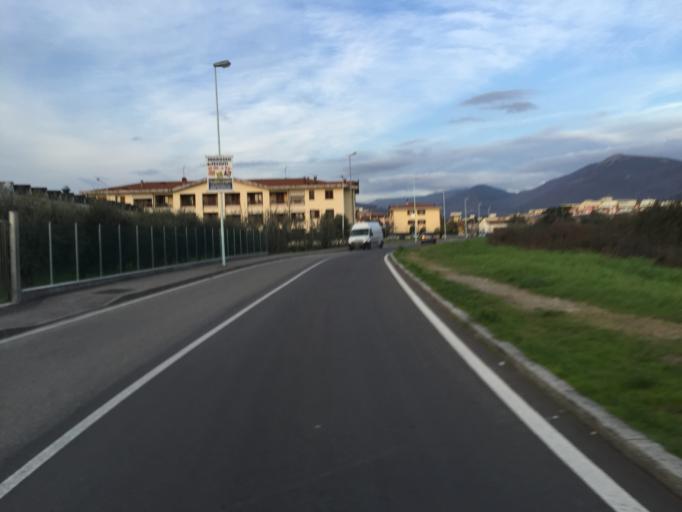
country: IT
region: Tuscany
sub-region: Provincia di Prato
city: Prato
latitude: 43.8809
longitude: 11.0796
